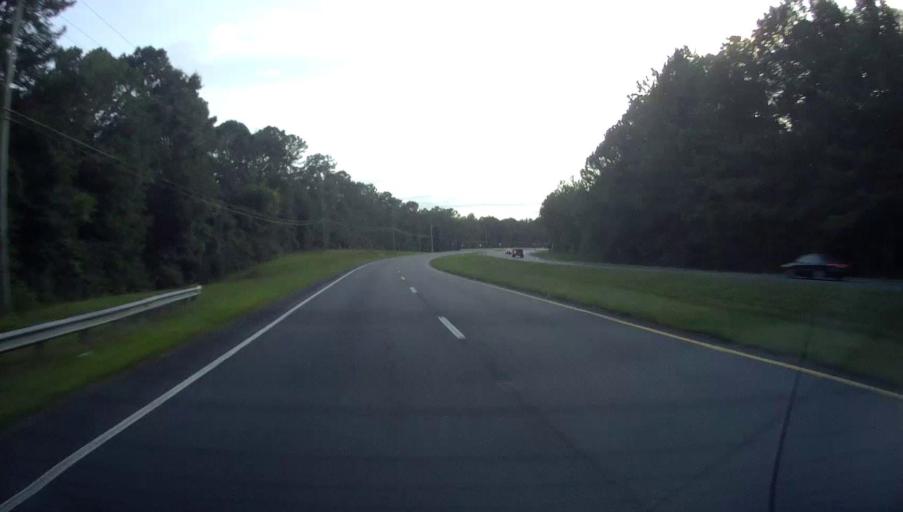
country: US
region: Georgia
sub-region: Muscogee County
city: Columbus
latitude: 32.5421
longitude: -84.8162
